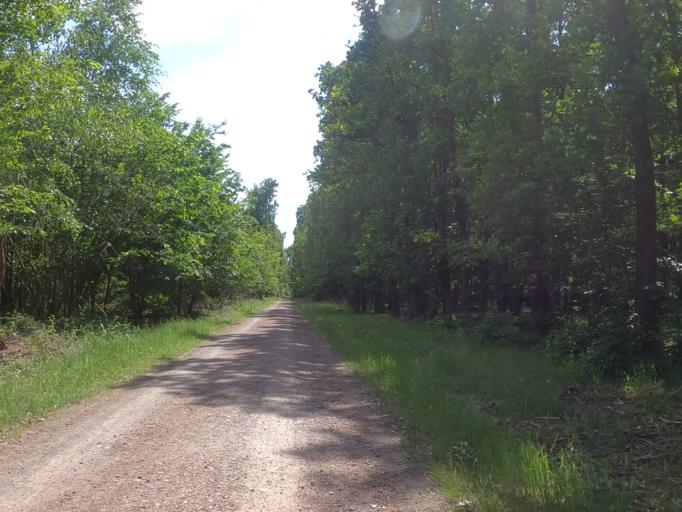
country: DE
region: Hesse
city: Morfelden-Walldorf
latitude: 49.9788
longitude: 8.5433
